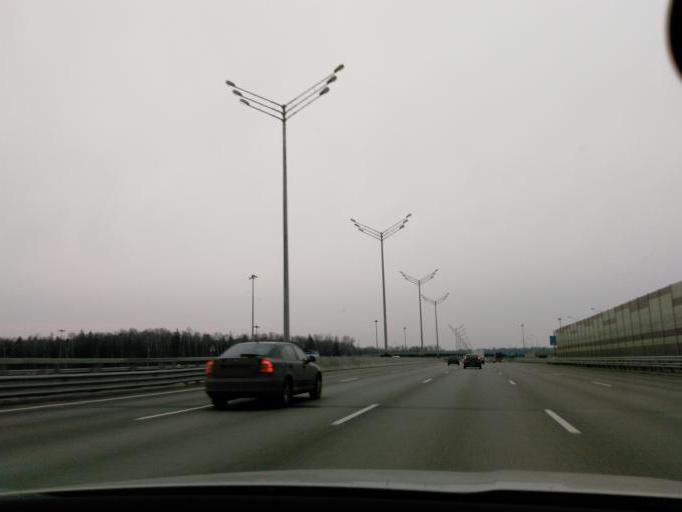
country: RU
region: Moscow
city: Khimki
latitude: 55.9581
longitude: 37.4104
